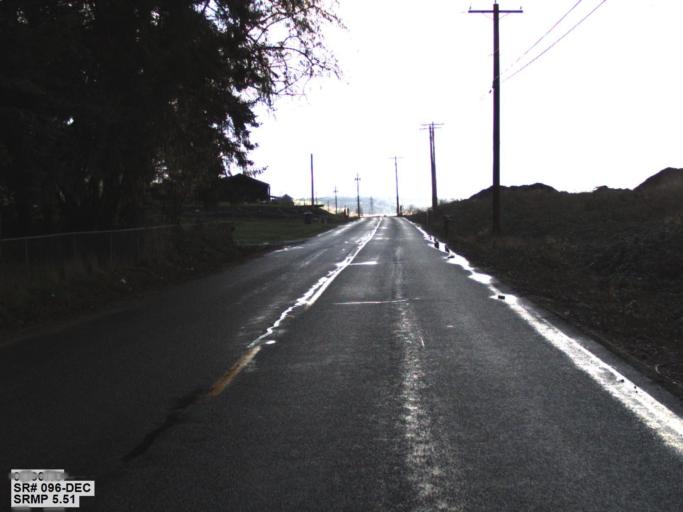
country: US
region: Washington
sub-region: Snohomish County
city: Silver Firs
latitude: 47.8848
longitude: -122.1331
